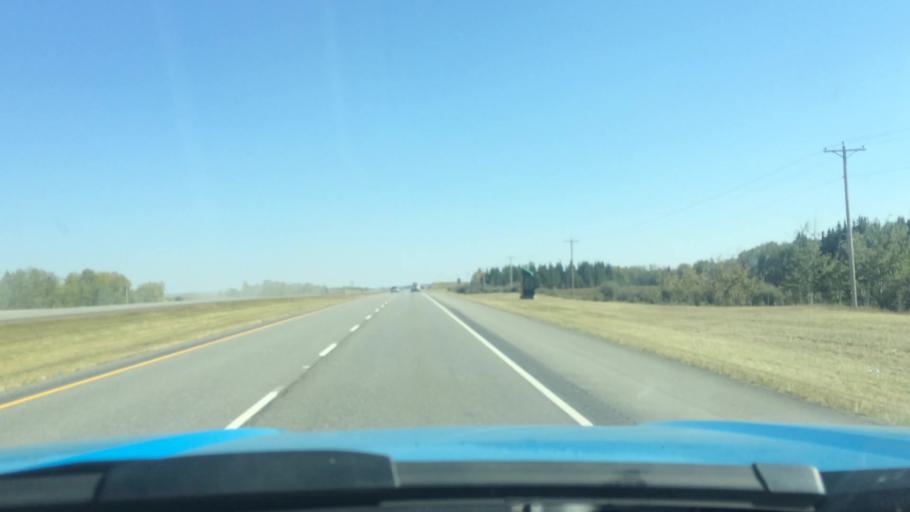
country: CA
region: Alberta
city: Cochrane
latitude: 51.1261
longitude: -114.6821
